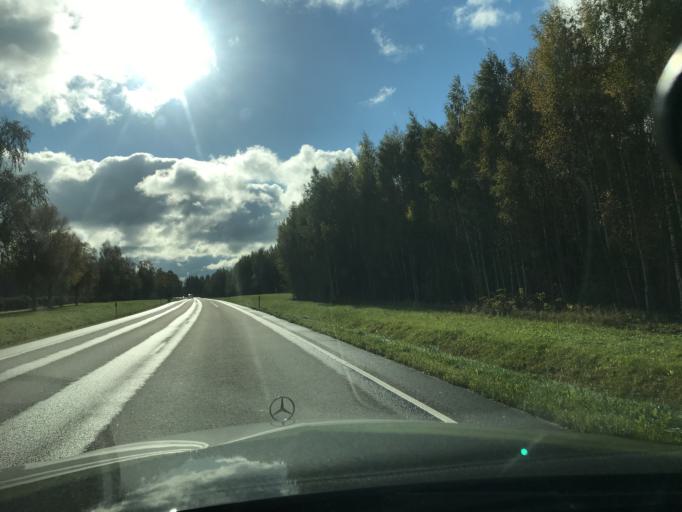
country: EE
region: Valgamaa
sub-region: Torva linn
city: Torva
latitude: 57.9852
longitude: 25.9433
